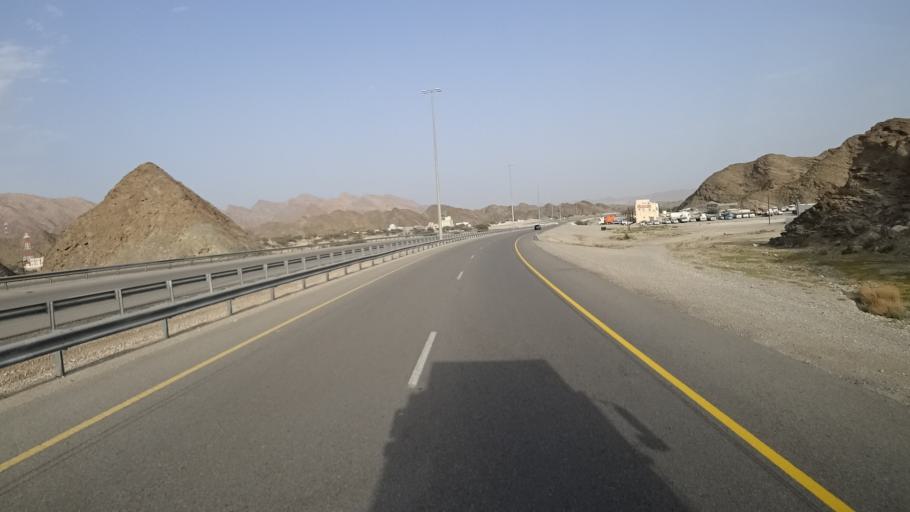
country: OM
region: Muhafazat Masqat
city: Bawshar
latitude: 23.3502
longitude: 58.5464
